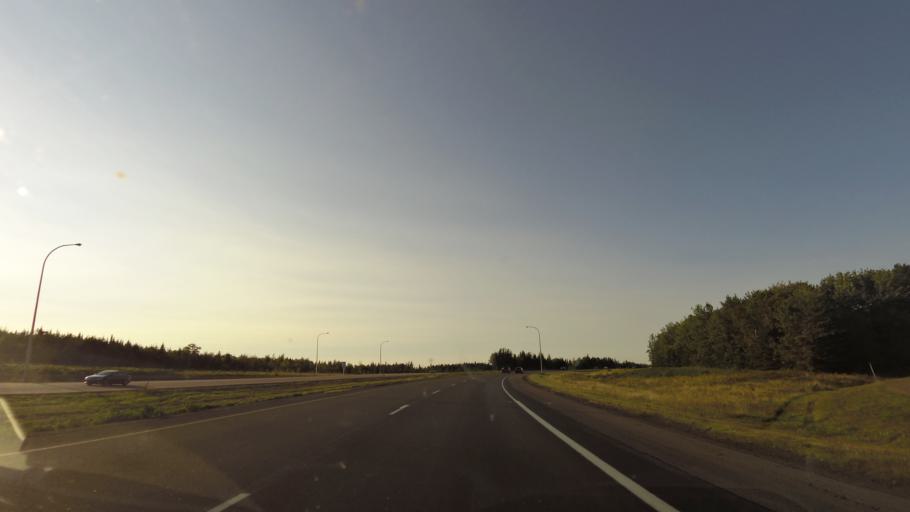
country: CA
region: New Brunswick
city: Dieppe
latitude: 46.0502
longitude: -64.5842
